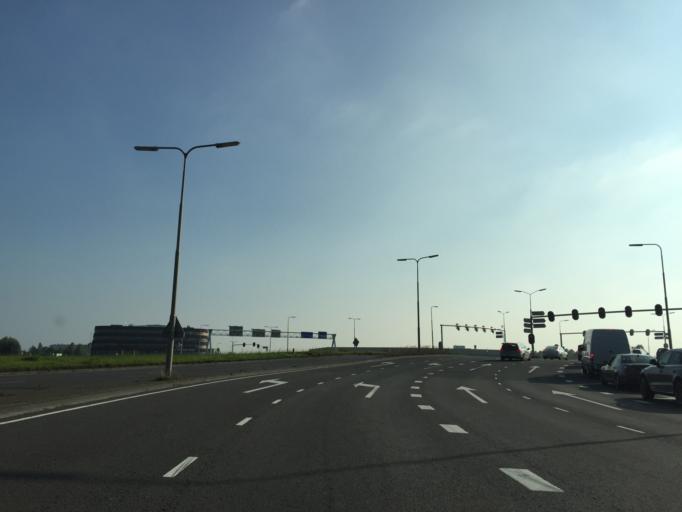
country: NL
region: South Holland
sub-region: Gemeente Barendrecht
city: Barendrecht
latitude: 51.8673
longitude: 4.5549
